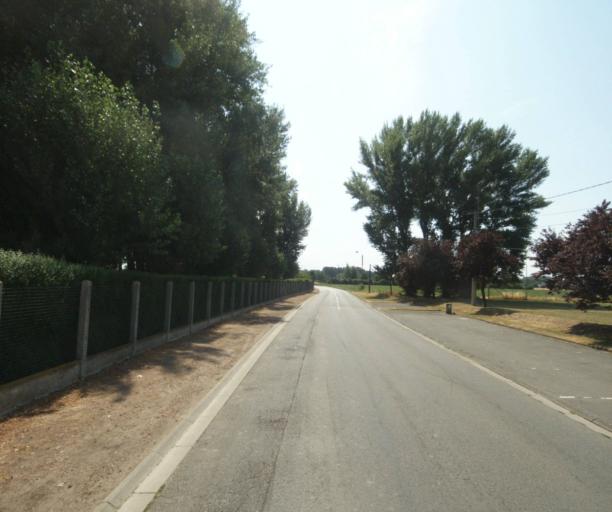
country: FR
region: Nord-Pas-de-Calais
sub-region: Departement du Nord
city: Comines
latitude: 50.7567
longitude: 3.0236
